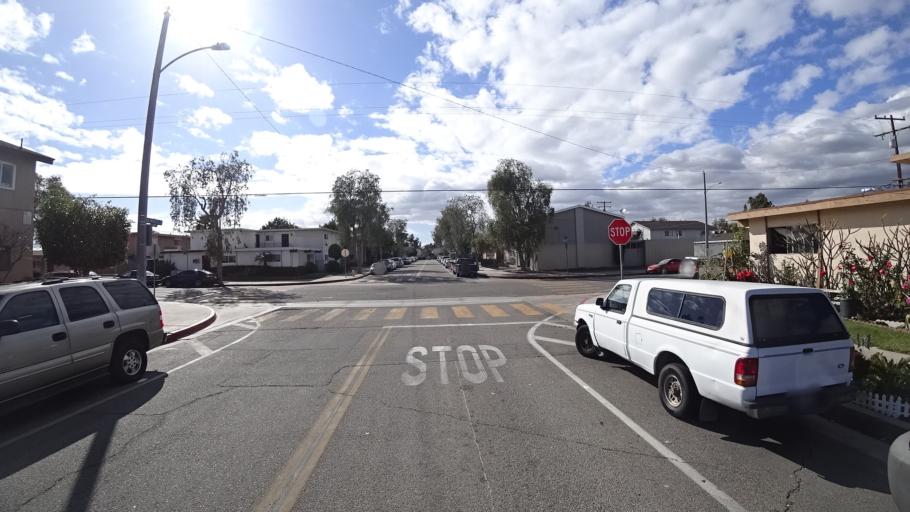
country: US
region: California
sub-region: Orange County
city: Anaheim
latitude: 33.8371
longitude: -117.9565
